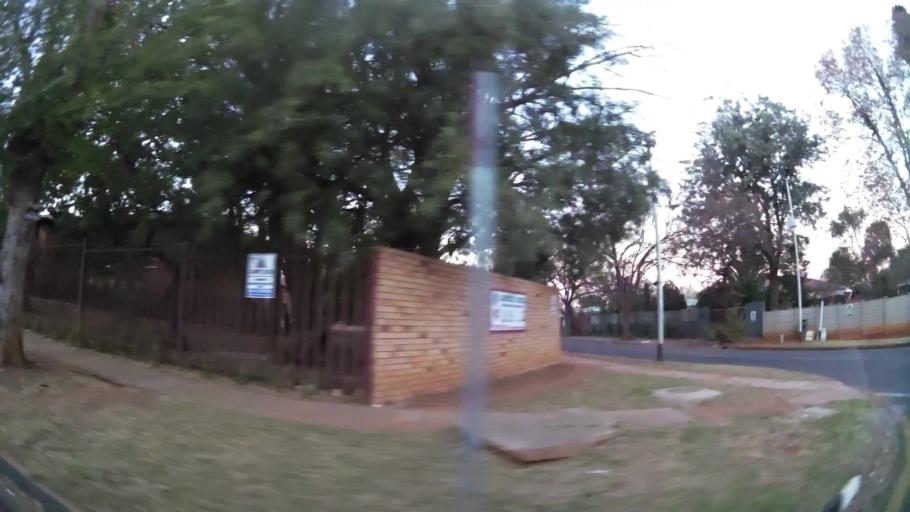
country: ZA
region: Gauteng
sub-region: City of Johannesburg Metropolitan Municipality
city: Roodepoort
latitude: -26.1729
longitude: 27.9237
